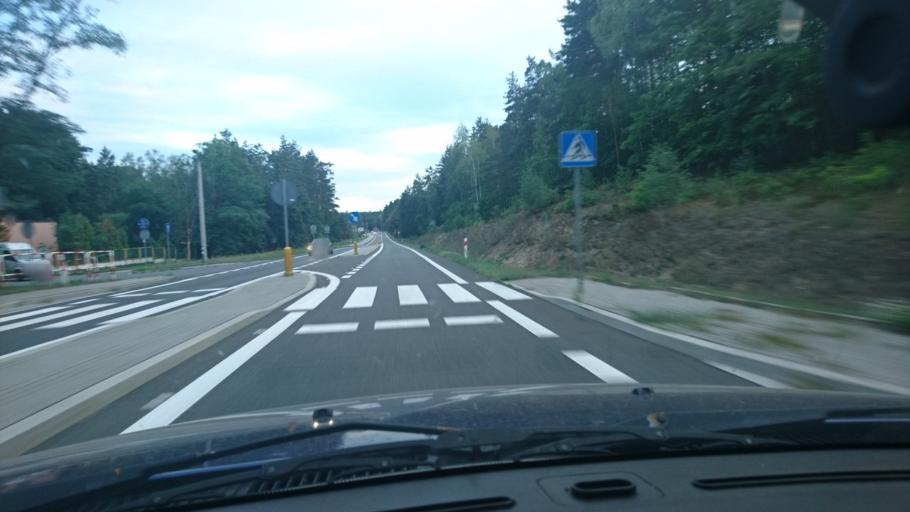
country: PL
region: Silesian Voivodeship
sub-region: Powiat tarnogorski
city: Tworog
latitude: 50.5961
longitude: 18.7023
